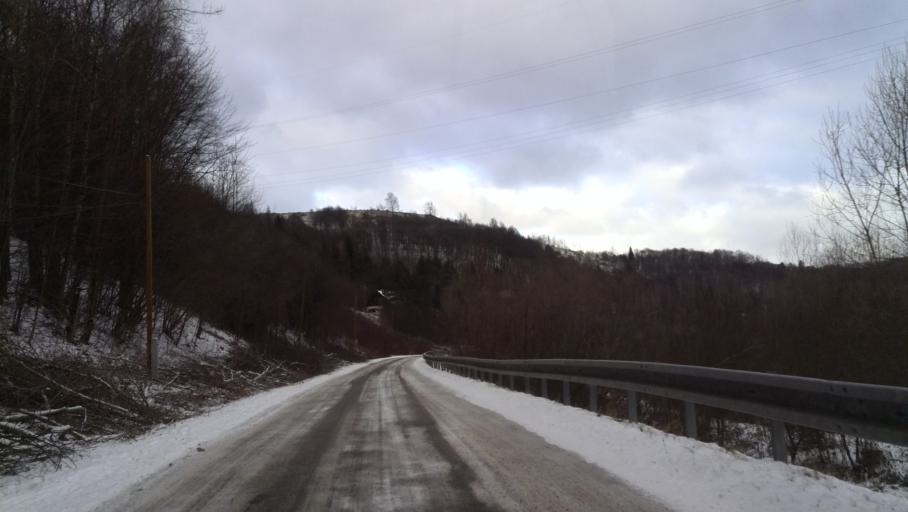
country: SK
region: Kosicky
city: Gelnica
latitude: 48.8241
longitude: 21.0654
